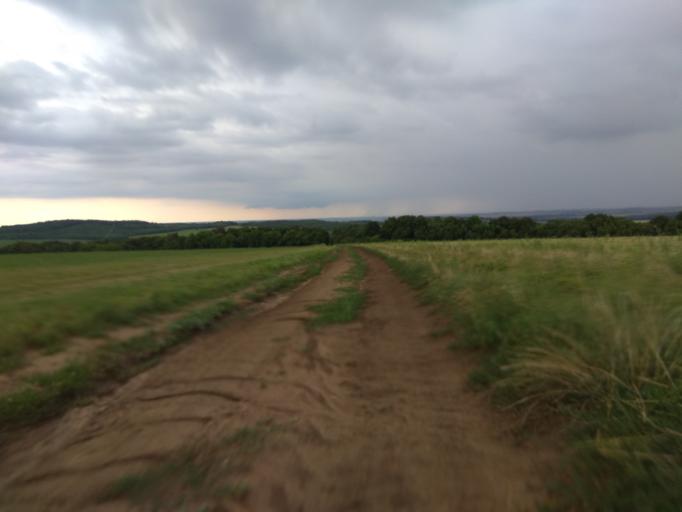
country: HU
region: Borsod-Abauj-Zemplen
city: Megyaszo
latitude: 48.1794
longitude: 21.0992
